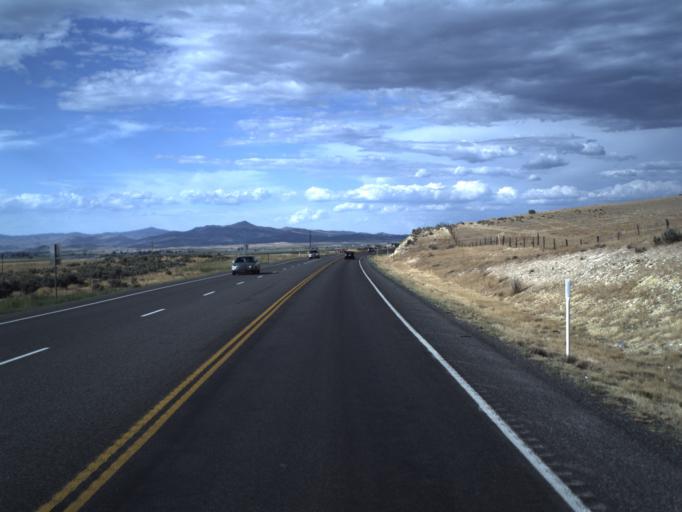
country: US
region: Utah
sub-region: Sanpete County
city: Ephraim
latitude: 39.4180
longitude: -111.5600
